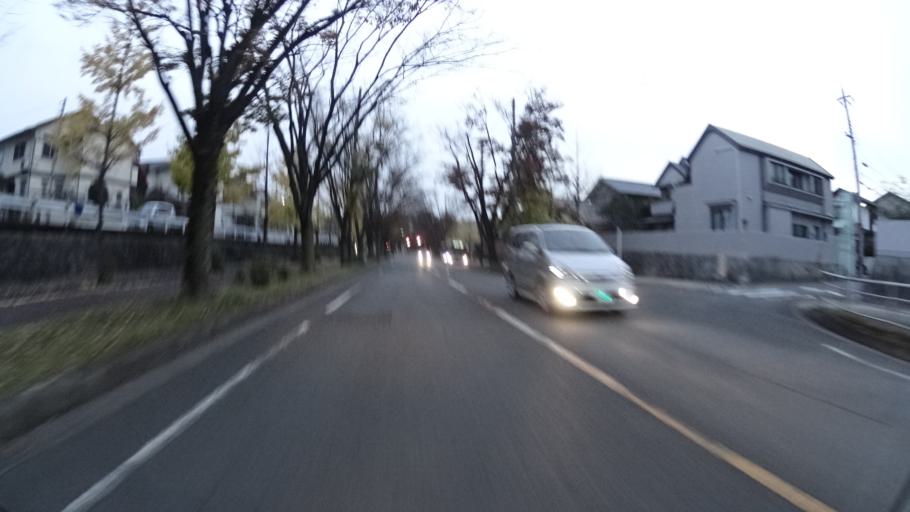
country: JP
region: Kyoto
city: Muko
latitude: 34.9579
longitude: 135.6698
